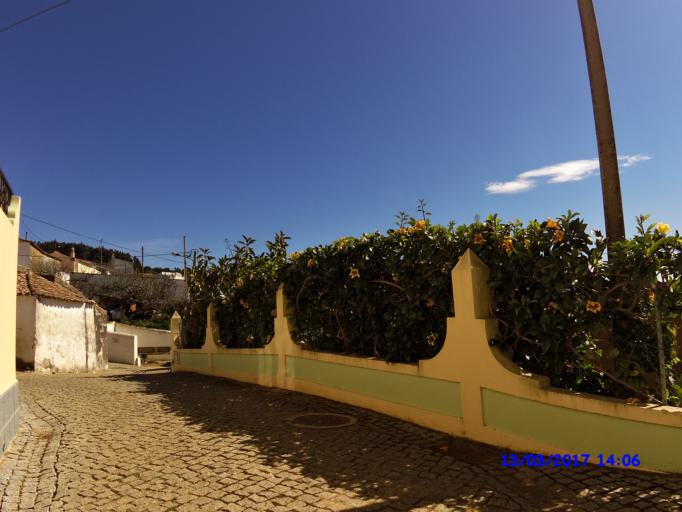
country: PT
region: Faro
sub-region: Monchique
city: Monchique
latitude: 37.3111
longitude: -8.6692
